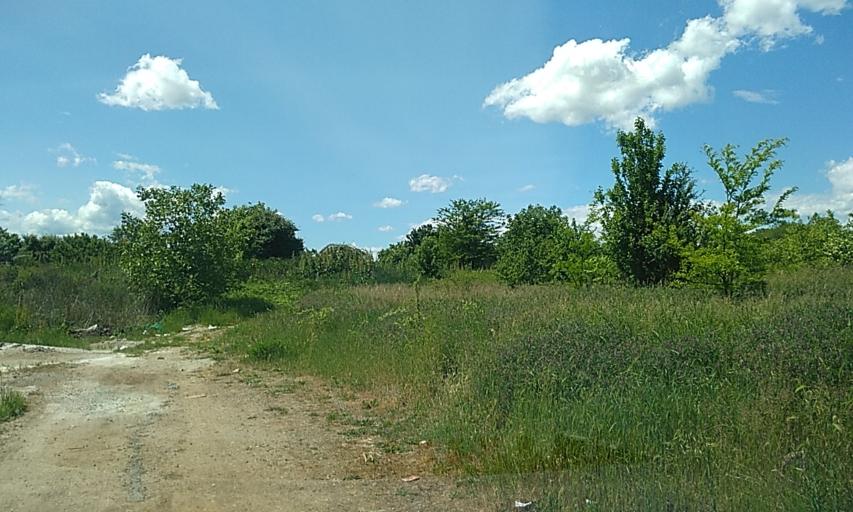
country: RS
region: Central Serbia
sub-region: Nisavski Okrug
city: Nis
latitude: 43.3369
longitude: 21.9045
